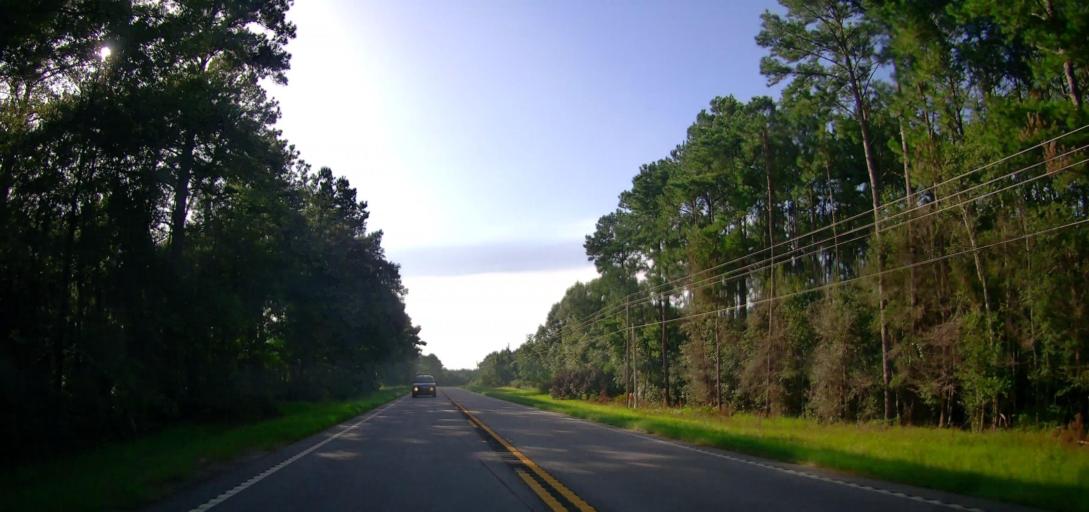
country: US
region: Georgia
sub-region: Coffee County
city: Nicholls
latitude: 31.3908
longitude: -82.6593
